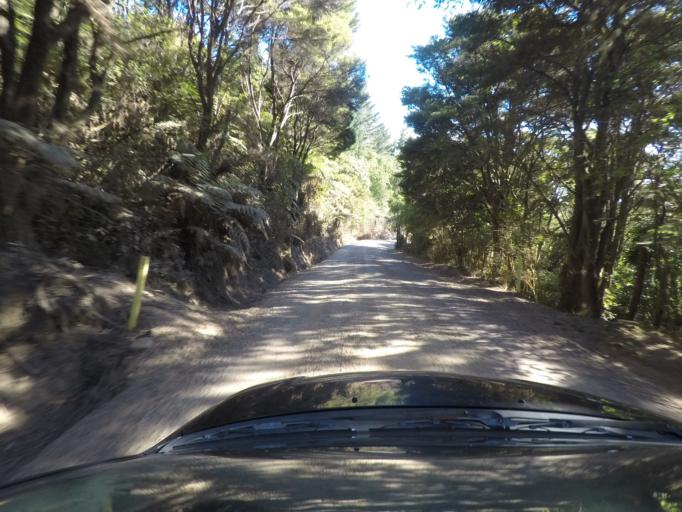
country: NZ
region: Northland
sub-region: Far North District
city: Paihia
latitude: -35.2552
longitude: 174.0709
